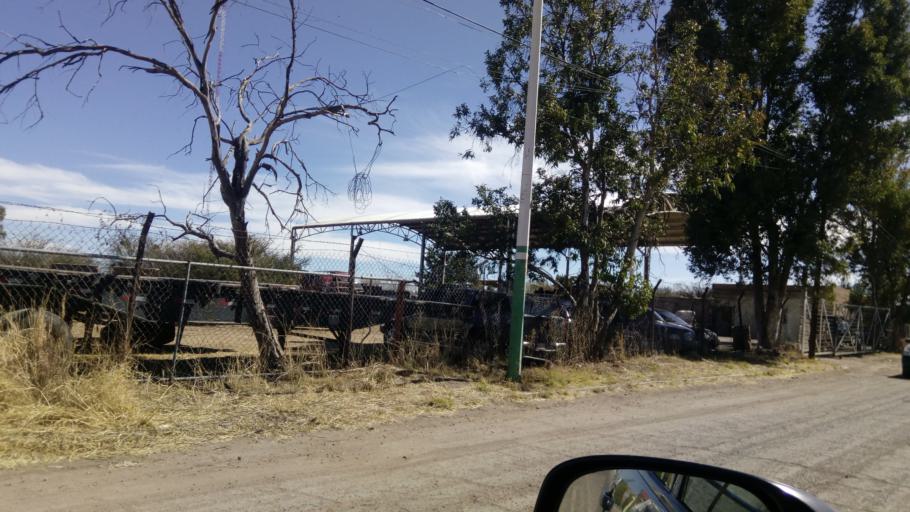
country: MX
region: Durango
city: Victoria de Durango
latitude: 24.0518
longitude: -104.6301
